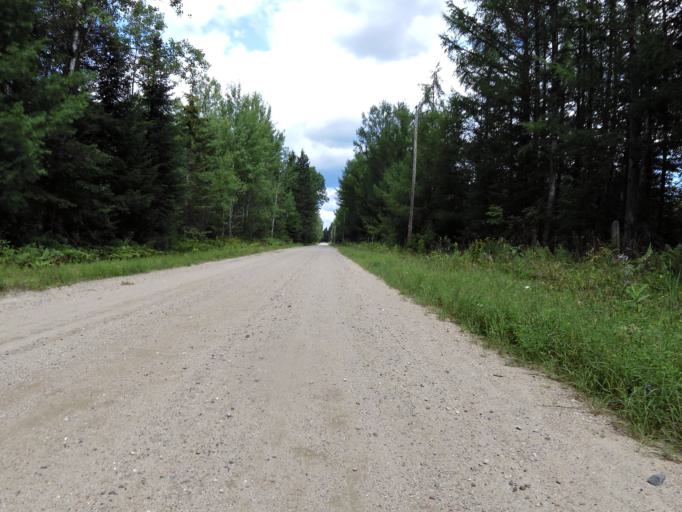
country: CA
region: Quebec
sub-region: Outaouais
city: Wakefield
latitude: 45.7716
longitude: -76.0306
